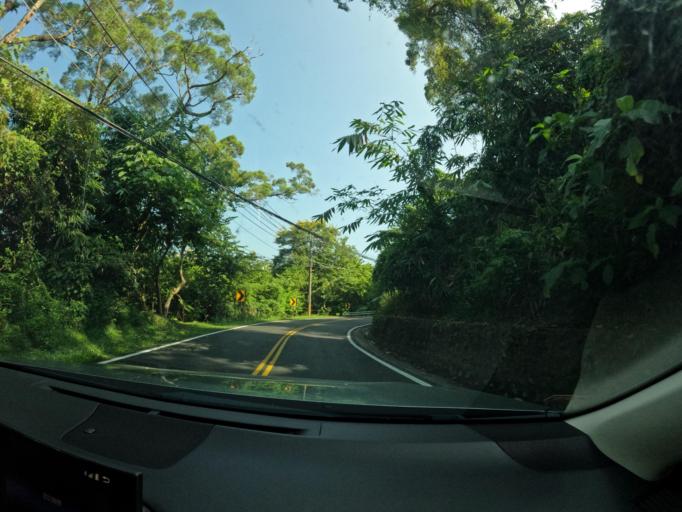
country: TW
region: Taiwan
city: Yujing
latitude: 23.0765
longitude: 120.6126
